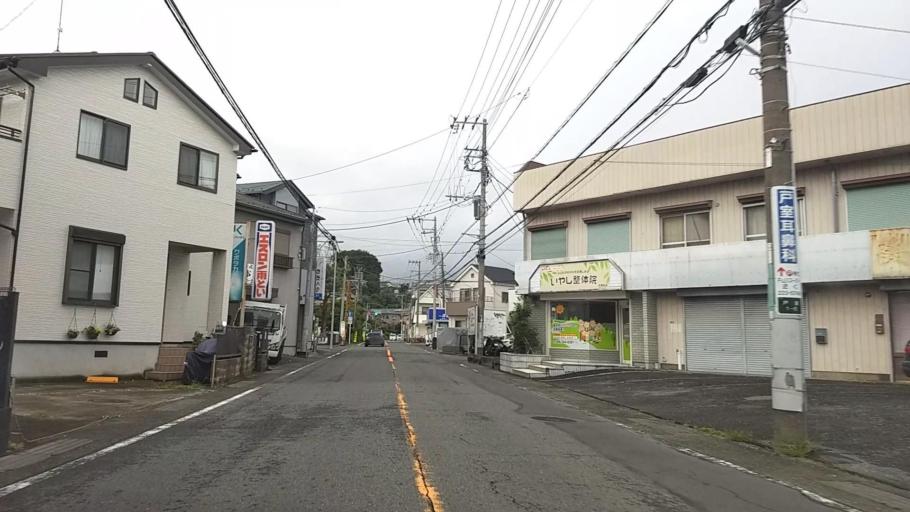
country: JP
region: Kanagawa
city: Atsugi
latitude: 35.4473
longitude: 139.3536
